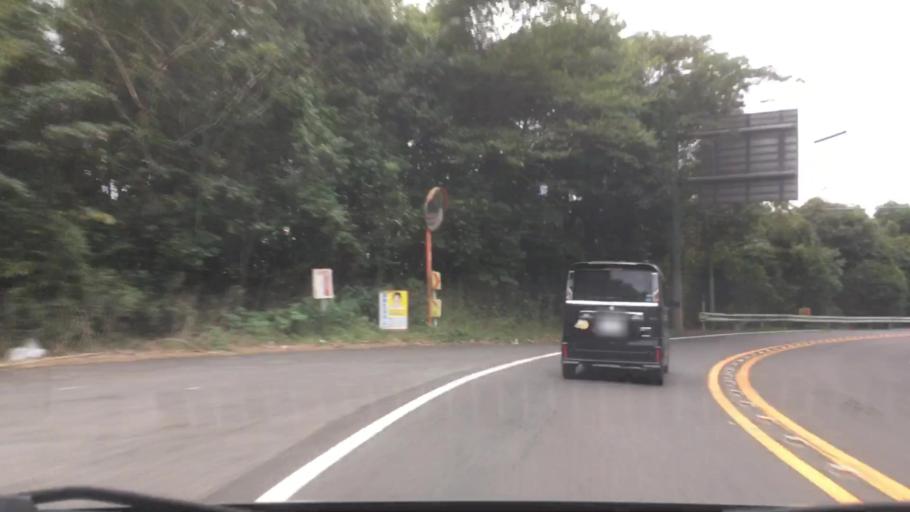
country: JP
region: Nagasaki
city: Sasebo
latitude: 33.0407
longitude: 129.7426
